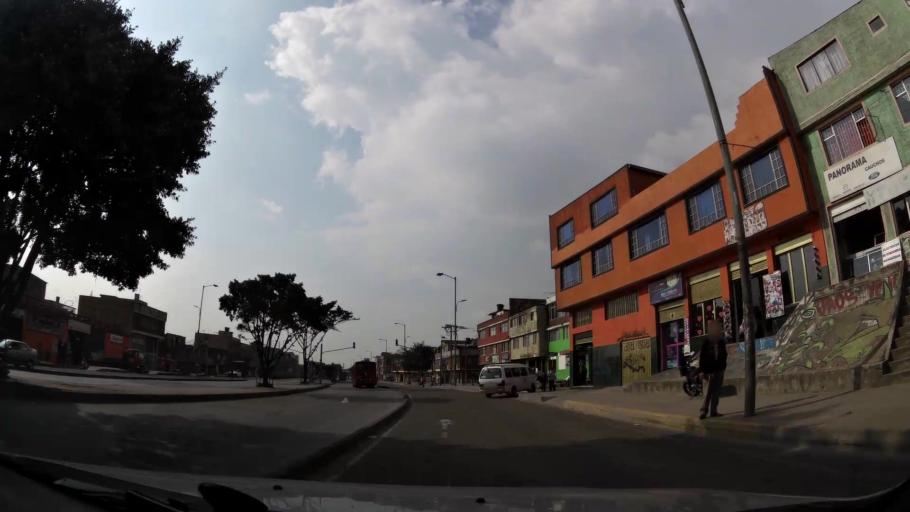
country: CO
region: Bogota D.C.
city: Bogota
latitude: 4.5636
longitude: -74.1250
